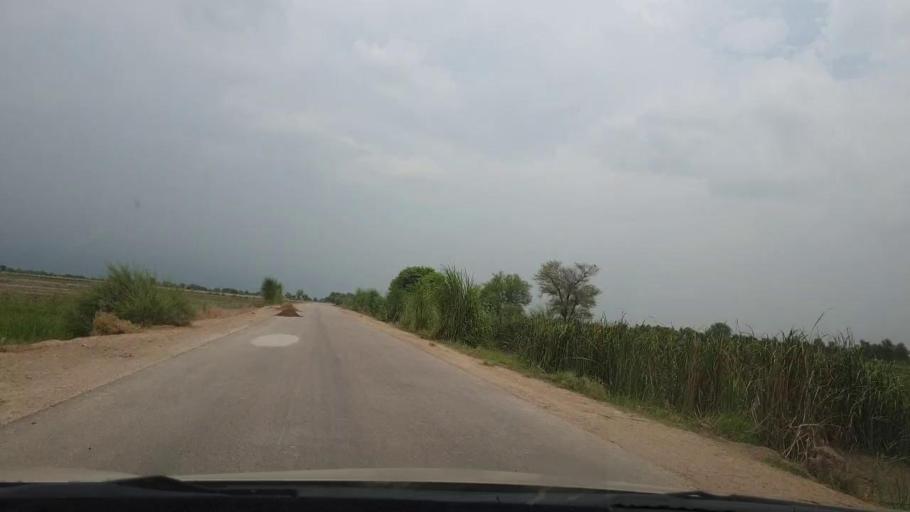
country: PK
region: Sindh
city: Ratodero
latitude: 27.8059
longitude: 68.3099
